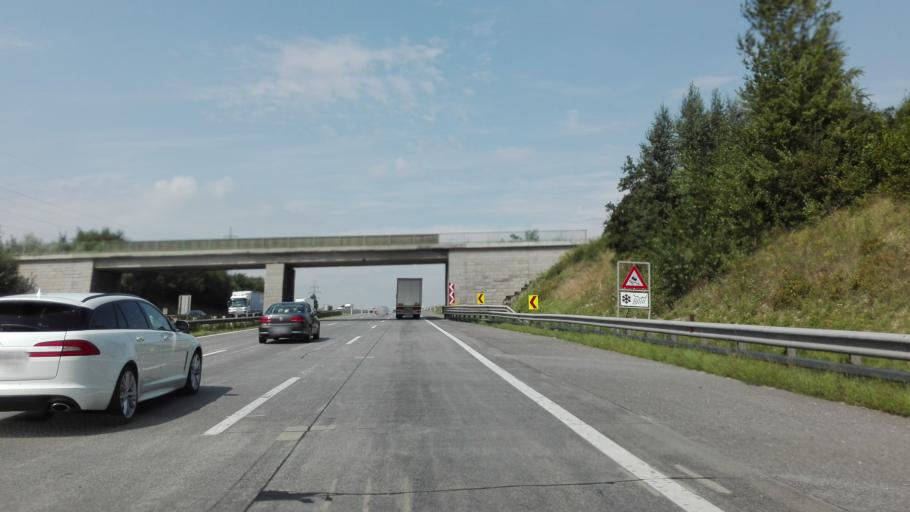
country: AT
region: Lower Austria
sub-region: Sankt Polten Stadt
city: Sankt Poelten
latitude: 48.1776
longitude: 15.6016
